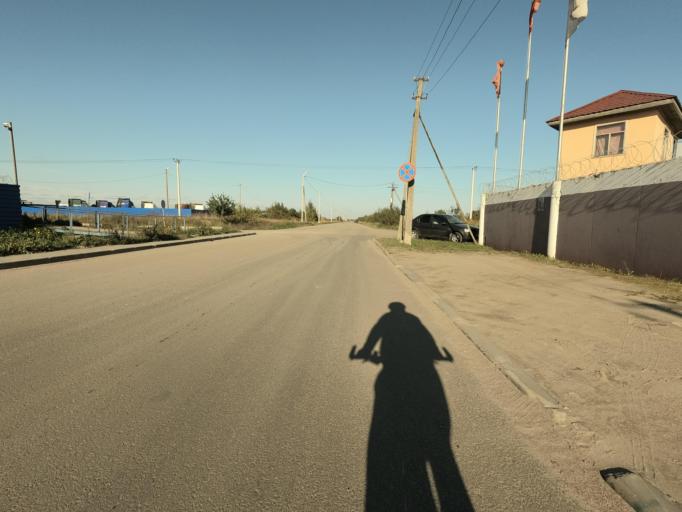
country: RU
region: St.-Petersburg
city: Petro-Slavyanka
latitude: 59.7645
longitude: 30.4850
